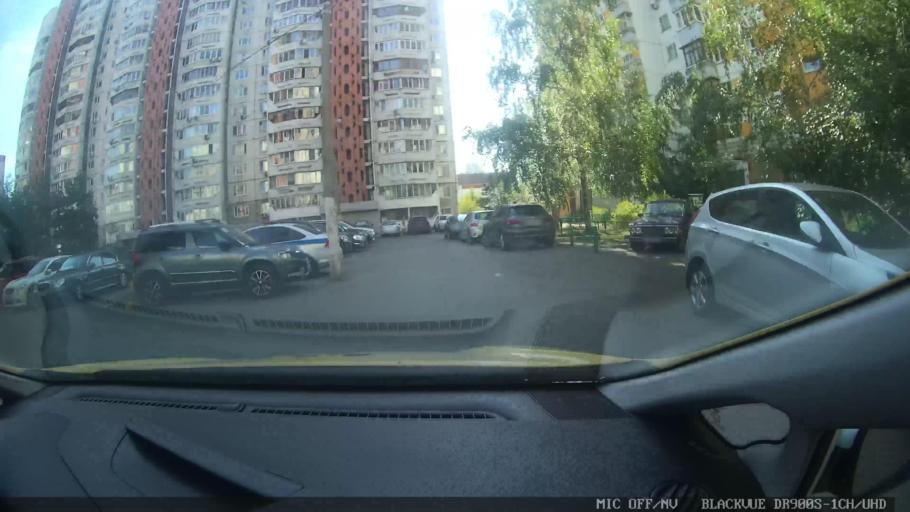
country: RU
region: Moscow
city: Zhulebino
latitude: 55.6817
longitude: 37.8629
